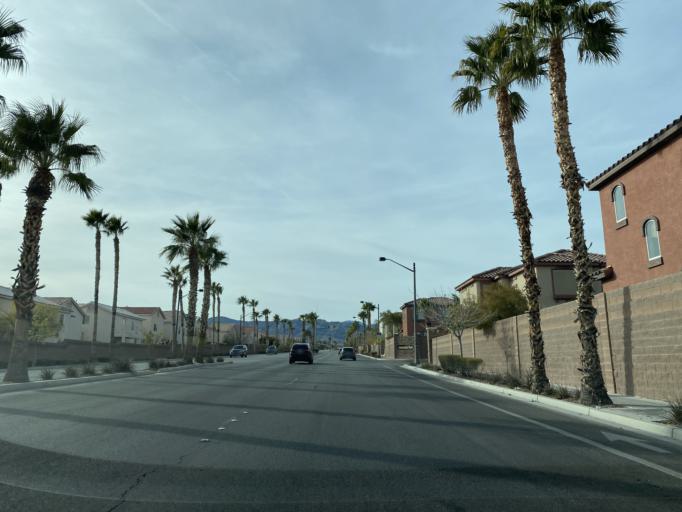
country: US
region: Nevada
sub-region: Clark County
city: Summerlin South
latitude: 36.2919
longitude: -115.2905
